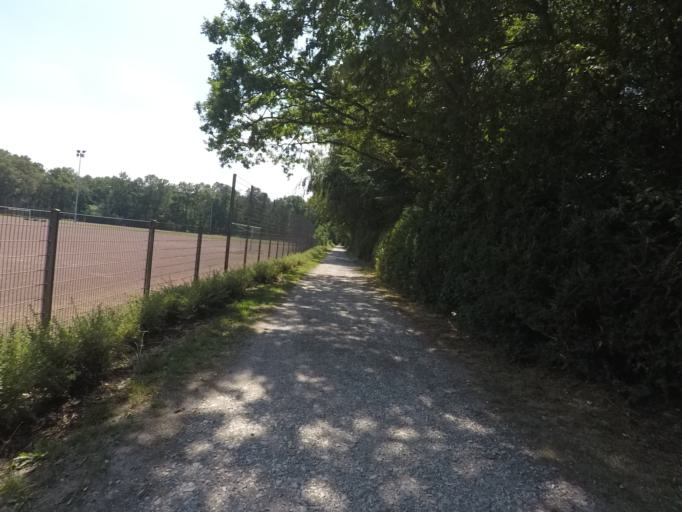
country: DE
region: North Rhine-Westphalia
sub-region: Regierungsbezirk Detmold
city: Bielefeld
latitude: 52.0365
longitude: 8.5777
